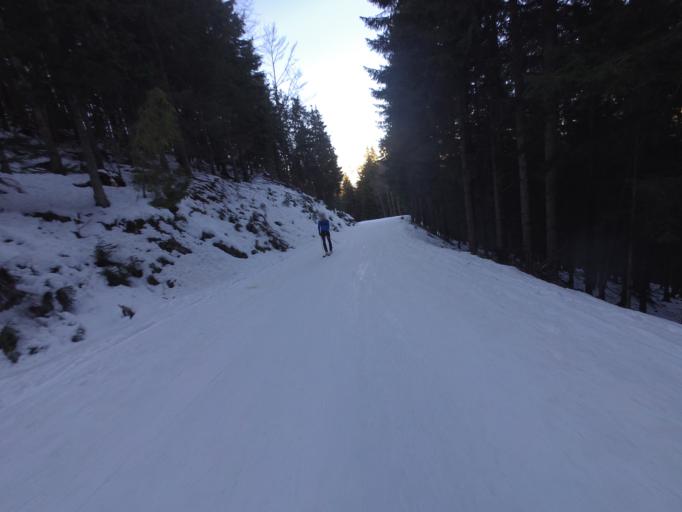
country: AT
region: Salzburg
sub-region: Politischer Bezirk Hallein
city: Scheffau am Tennengebirge
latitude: 47.6391
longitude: 13.2485
